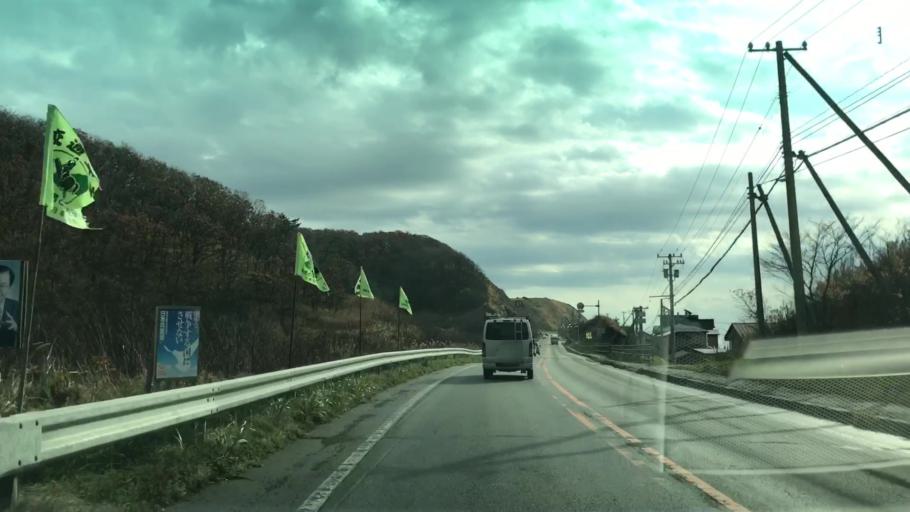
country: JP
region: Hokkaido
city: Shizunai-furukawacho
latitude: 42.1510
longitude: 142.8021
